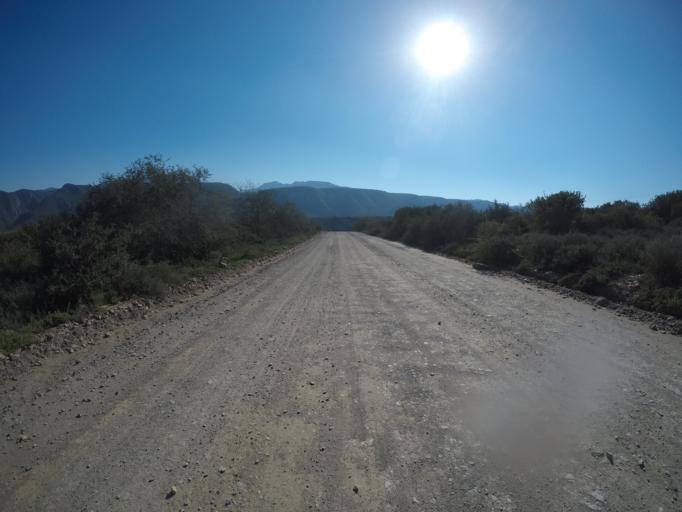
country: ZA
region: Eastern Cape
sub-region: Cacadu District Municipality
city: Kruisfontein
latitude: -33.6717
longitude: 24.5768
